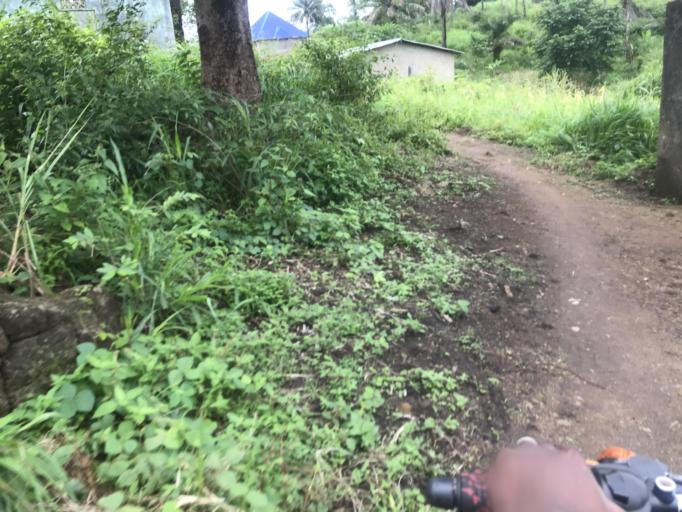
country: SL
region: Eastern Province
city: Buedu
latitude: 8.4606
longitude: -10.3277
